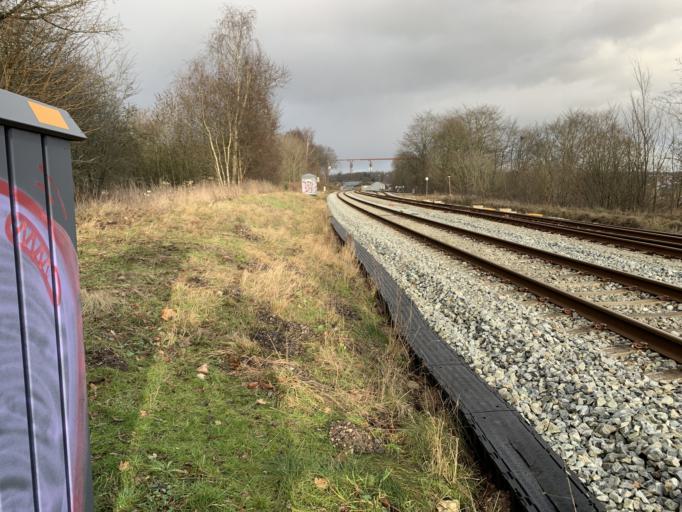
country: DK
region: North Denmark
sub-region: Mariagerfjord Kommune
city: Hobro
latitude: 56.6385
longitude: 9.7775
